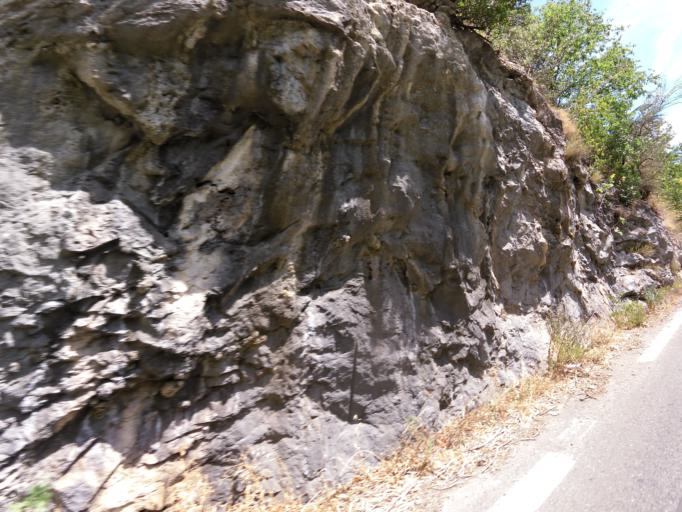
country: FR
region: Languedoc-Roussillon
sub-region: Departement de l'Herault
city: Ganges
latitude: 43.9372
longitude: 3.6956
